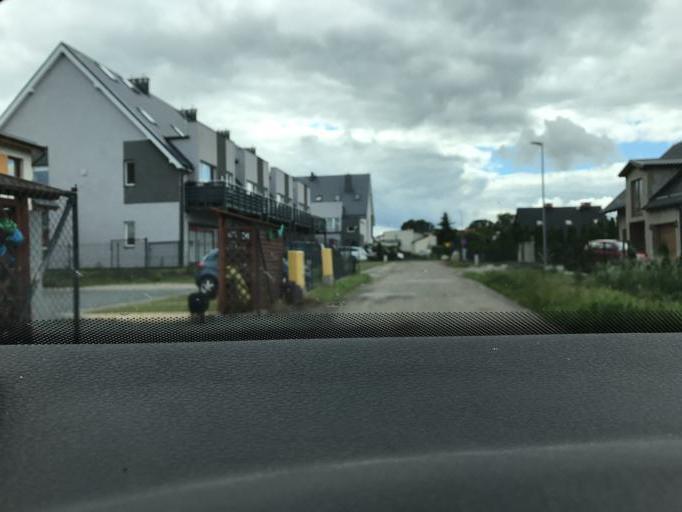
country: PL
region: Pomeranian Voivodeship
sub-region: Powiat gdanski
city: Pruszcz Gdanski
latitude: 54.2616
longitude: 18.6785
